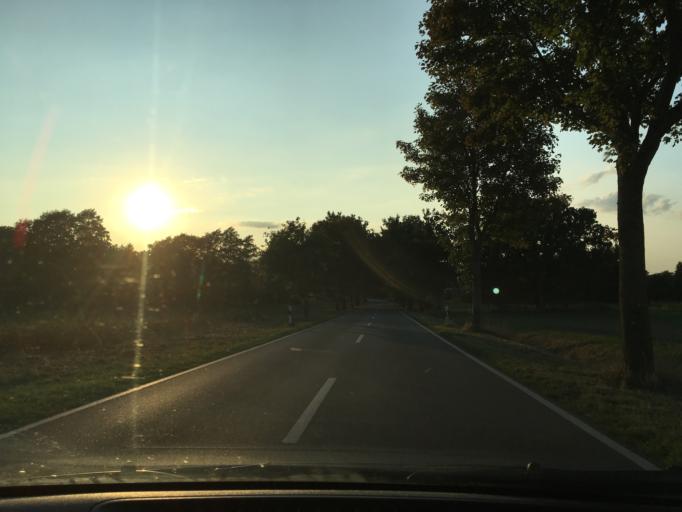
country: DE
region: Lower Saxony
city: Bleckede
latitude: 53.2593
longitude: 10.7495
